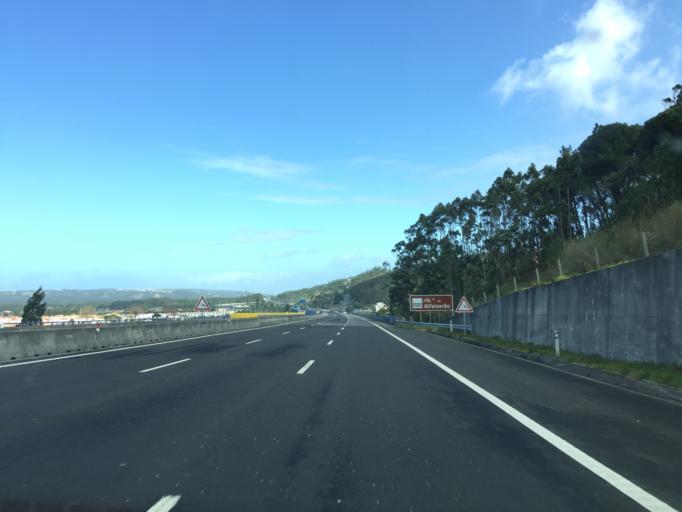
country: PT
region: Leiria
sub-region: Caldas da Rainha
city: Caldas da Rainha
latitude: 39.4914
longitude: -9.0941
